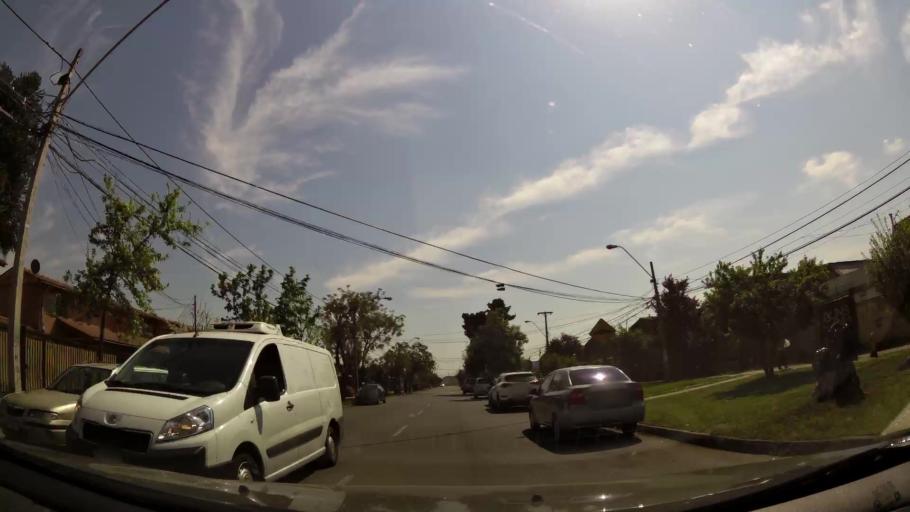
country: CL
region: Santiago Metropolitan
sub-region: Provincia de Cordillera
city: Puente Alto
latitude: -33.5799
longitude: -70.5926
